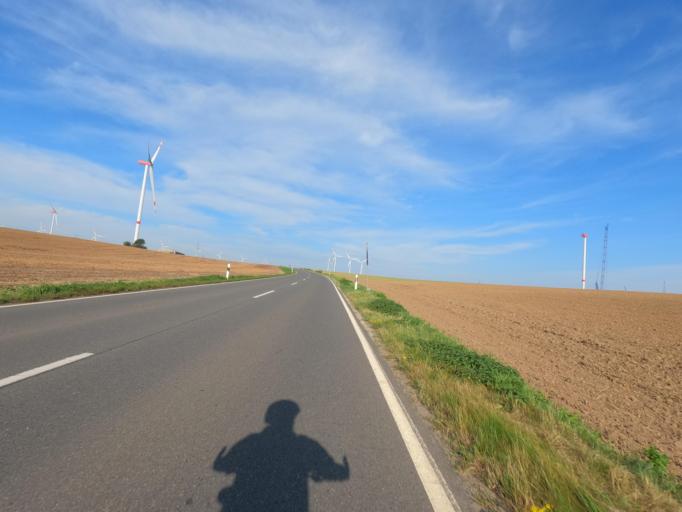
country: DE
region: North Rhine-Westphalia
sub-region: Regierungsbezirk Koln
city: Linnich
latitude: 50.9825
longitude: 6.2499
